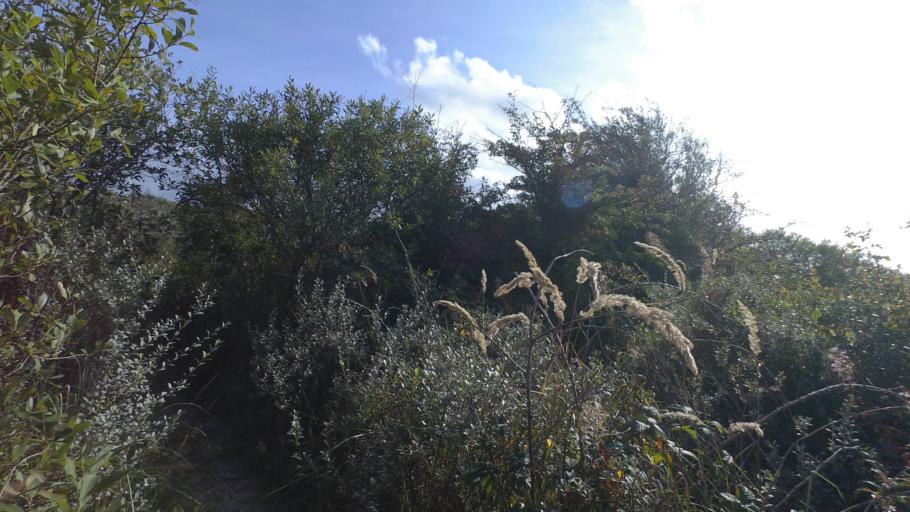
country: NL
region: Friesland
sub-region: Gemeente Ameland
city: Nes
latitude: 53.4561
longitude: 5.8375
